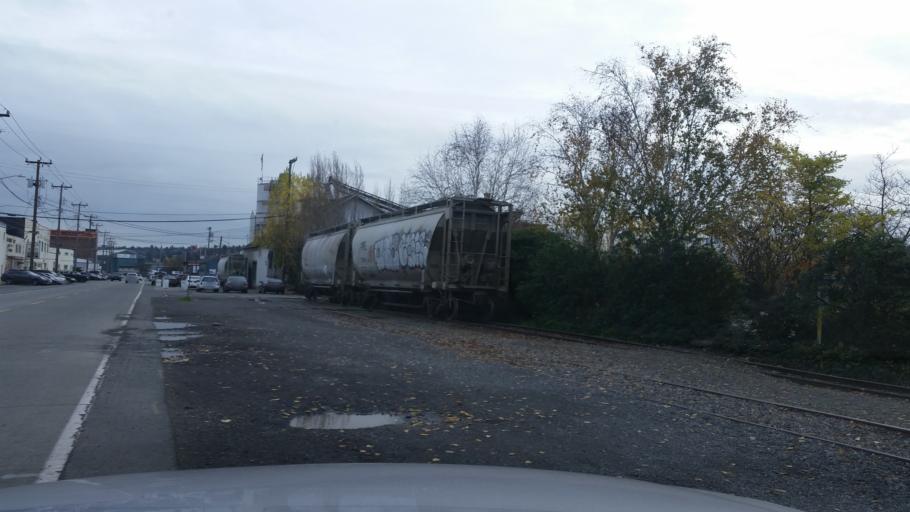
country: US
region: Washington
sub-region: King County
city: Seattle
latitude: 47.6661
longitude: -122.3842
